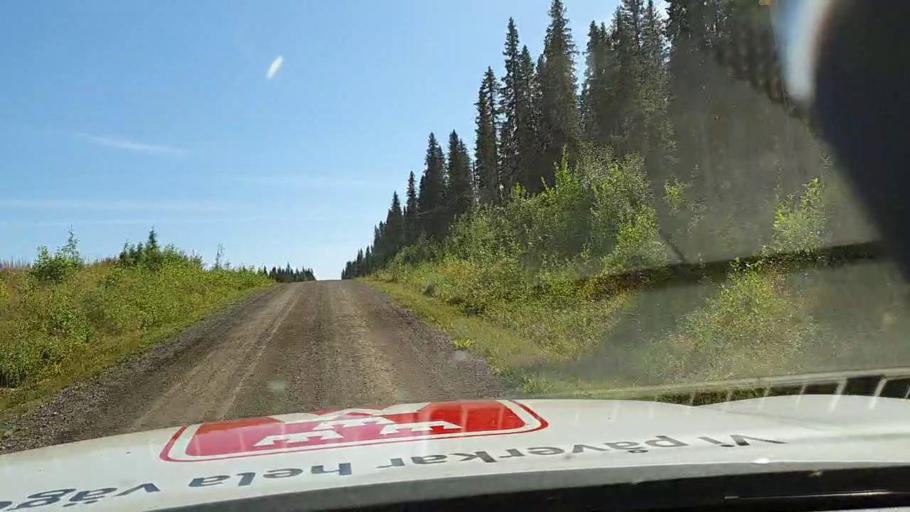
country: SE
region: Jaemtland
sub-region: Stroemsunds Kommun
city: Stroemsund
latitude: 63.7846
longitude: 15.3040
